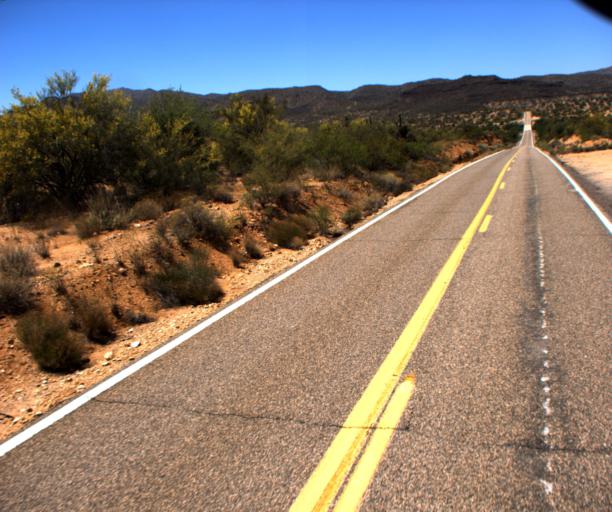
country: US
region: Arizona
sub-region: Yavapai County
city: Bagdad
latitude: 34.4765
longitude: -113.0564
